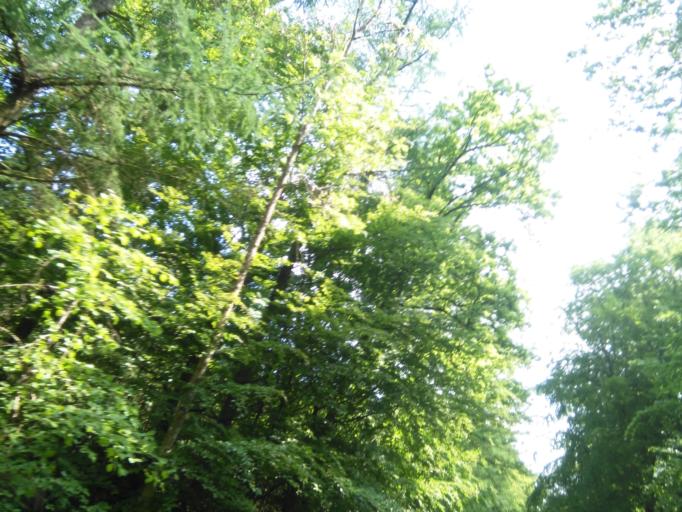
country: DK
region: Central Jutland
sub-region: Favrskov Kommune
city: Hinnerup
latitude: 56.2760
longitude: 9.9979
